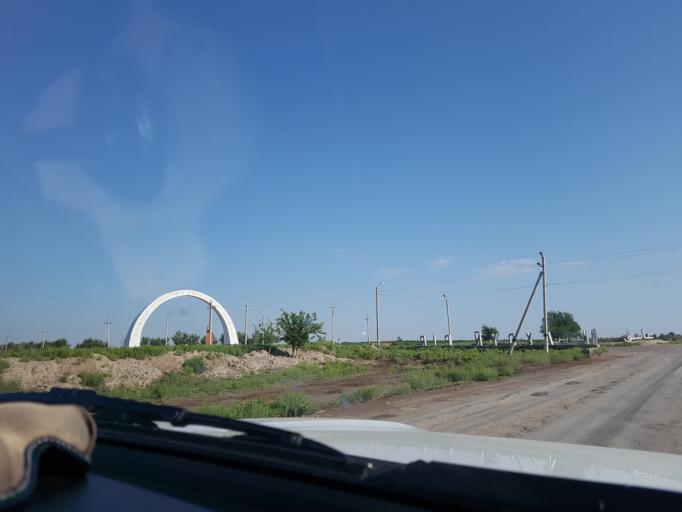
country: TM
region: Dasoguz
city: Koeneuergench
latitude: 41.8621
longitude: 58.7055
